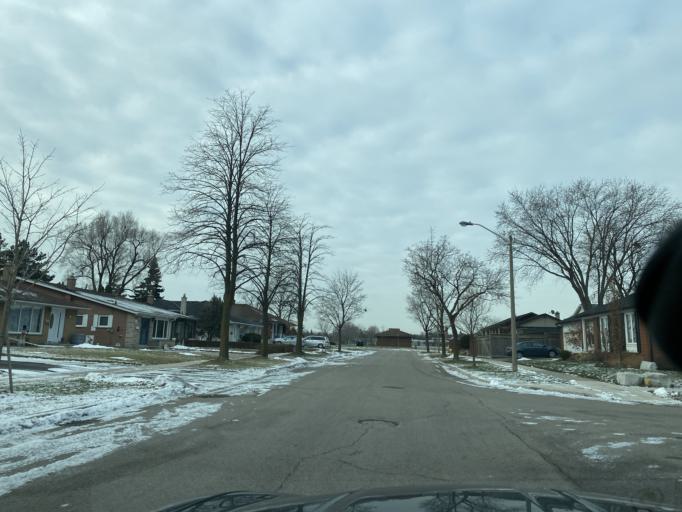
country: CA
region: Ontario
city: Etobicoke
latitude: 43.6575
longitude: -79.5722
